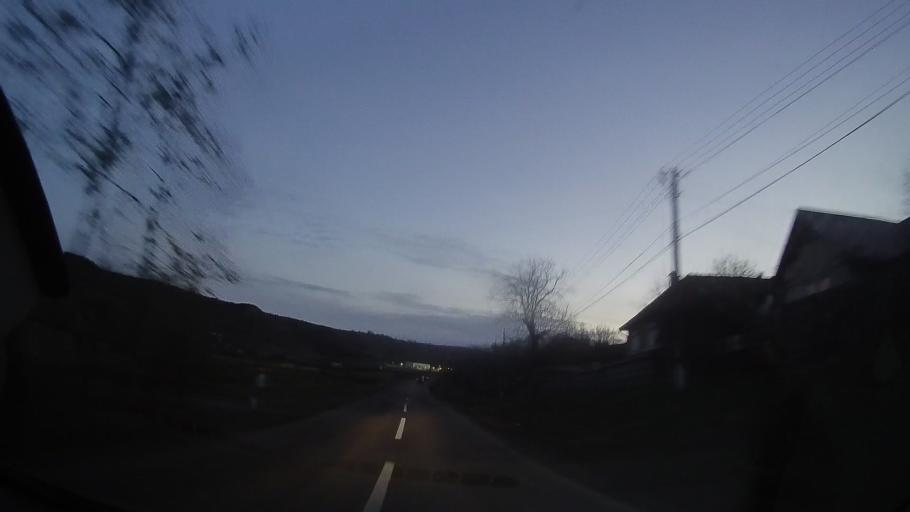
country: RO
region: Mures
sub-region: Comuna Sarmasu
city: Sarmasu
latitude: 46.7800
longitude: 24.2025
